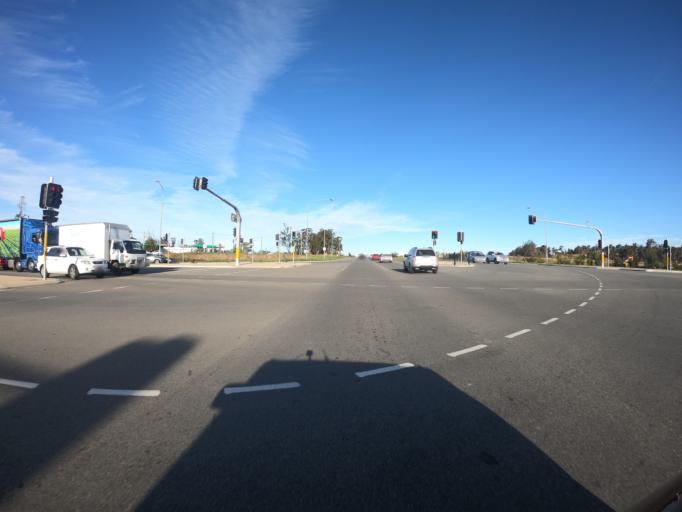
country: AU
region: New South Wales
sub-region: Blacktown
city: Hassall Grove
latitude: -33.6968
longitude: 150.8311
